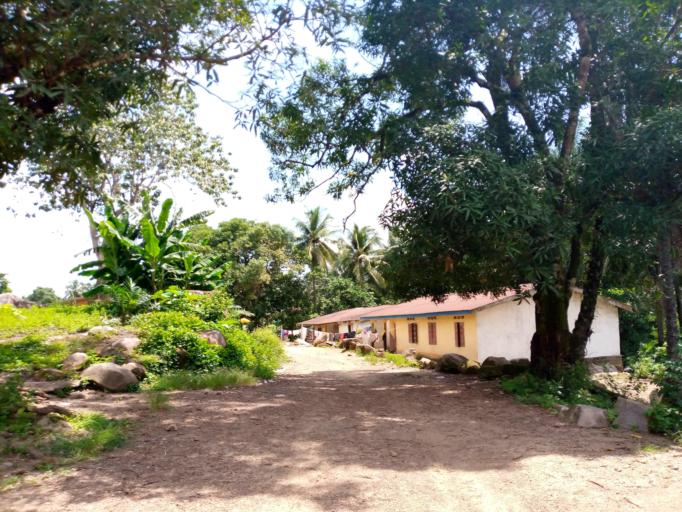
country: SL
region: Northern Province
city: Magburaka
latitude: 8.7269
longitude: -11.9440
